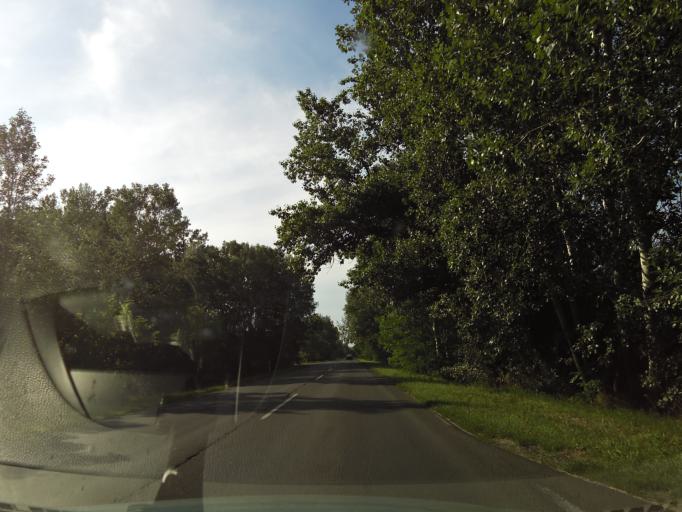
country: HU
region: Csongrad
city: Szatymaz
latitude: 46.3585
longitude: 20.0511
